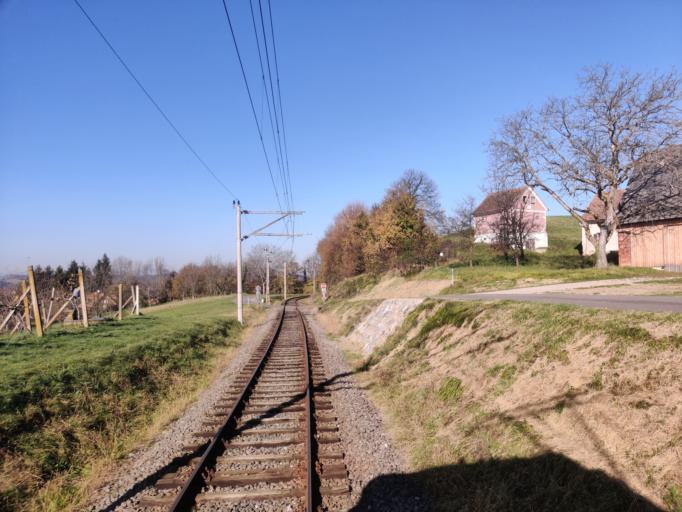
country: AT
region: Styria
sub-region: Politischer Bezirk Suedoststeiermark
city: Maierdorf
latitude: 46.8967
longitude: 15.8334
